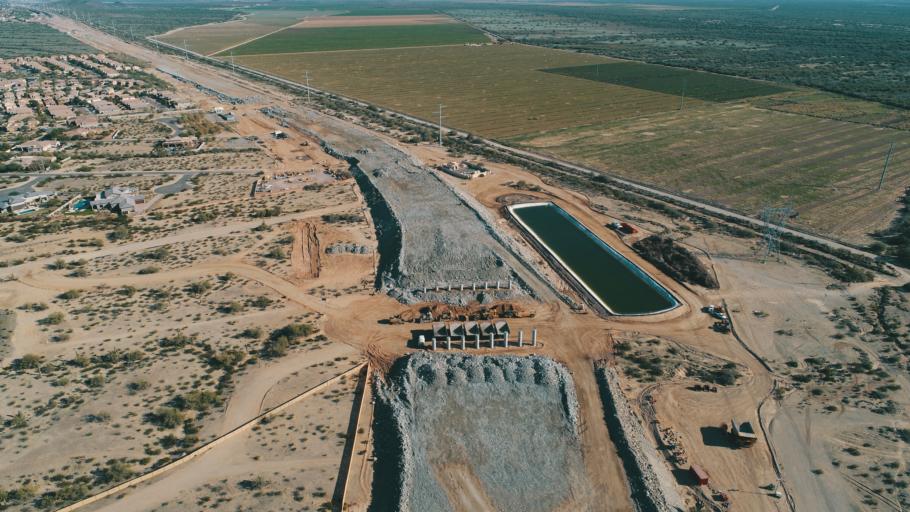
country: US
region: Arizona
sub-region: Maricopa County
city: Laveen
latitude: 33.2937
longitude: -112.1348
